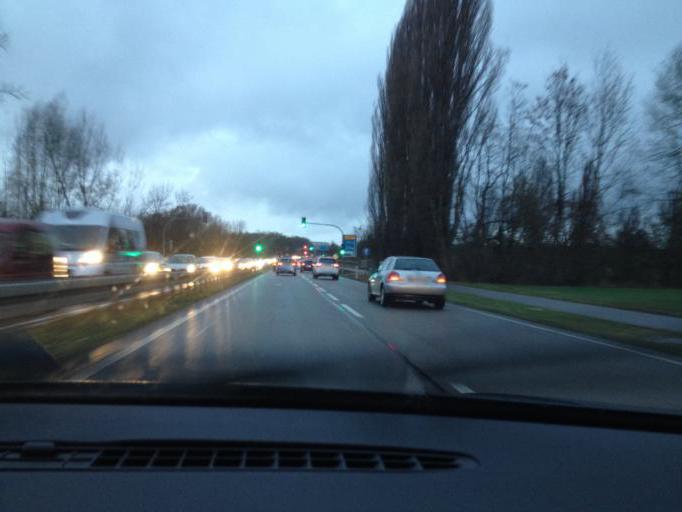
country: DE
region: Baden-Wuerttemberg
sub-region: Regierungsbezirk Stuttgart
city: Asperg
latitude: 48.9150
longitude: 9.1634
